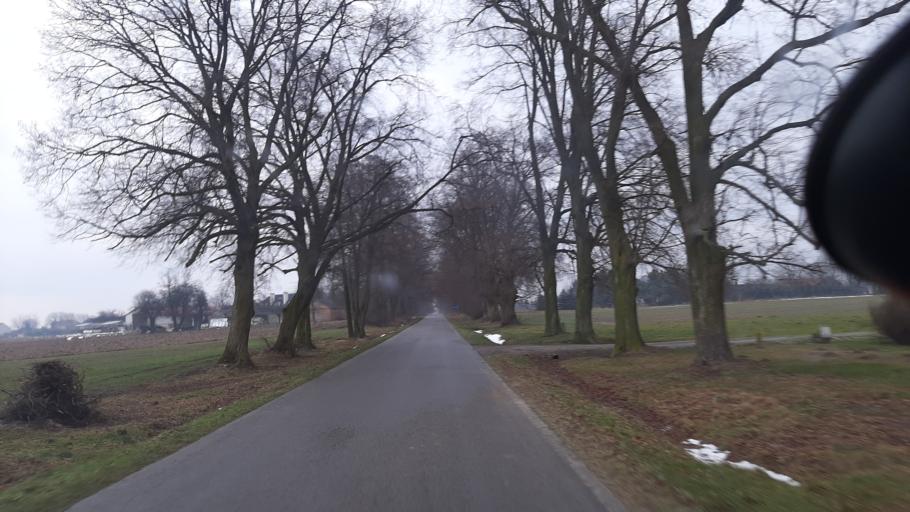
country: PL
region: Lublin Voivodeship
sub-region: Powiat lubelski
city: Lublin
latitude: 51.3422
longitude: 22.5321
